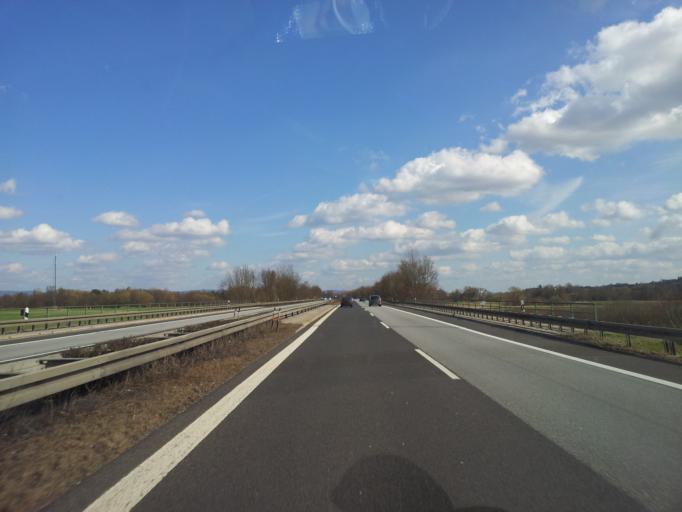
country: DE
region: Bavaria
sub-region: Upper Franconia
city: Bischberg
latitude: 49.9214
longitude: 10.8302
